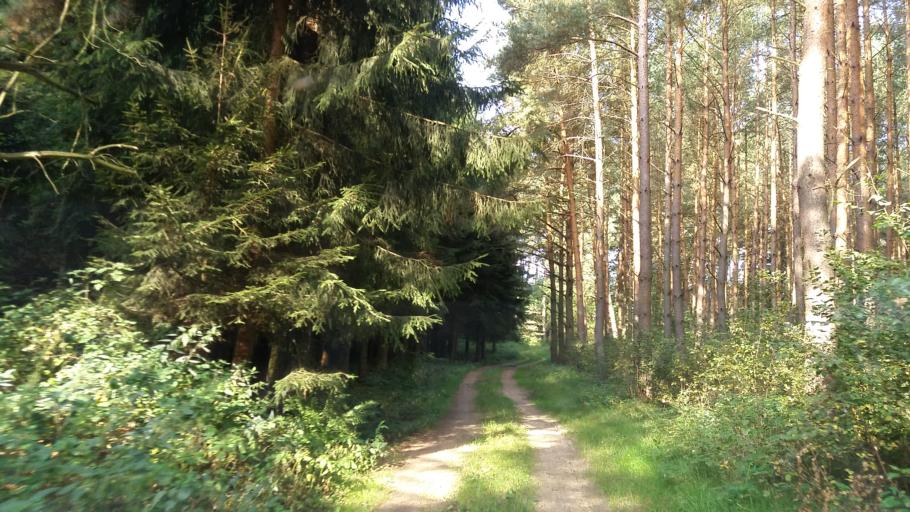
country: PL
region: West Pomeranian Voivodeship
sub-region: Powiat stargardzki
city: Suchan
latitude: 53.2458
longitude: 15.3679
